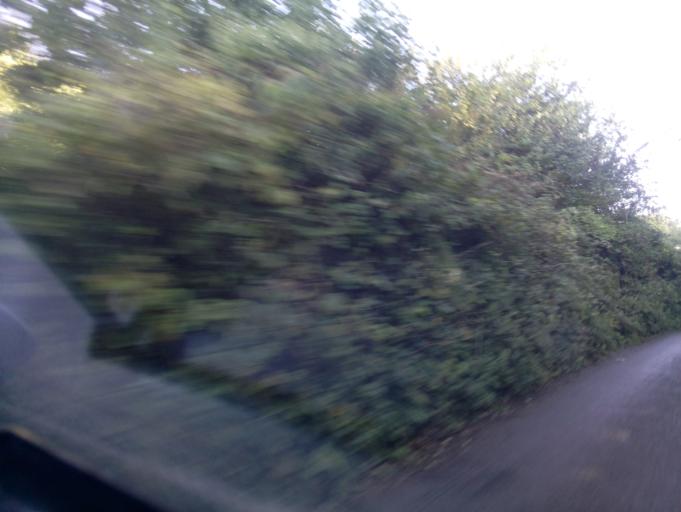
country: GB
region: England
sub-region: Devon
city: Totnes
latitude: 50.3453
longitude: -3.6912
